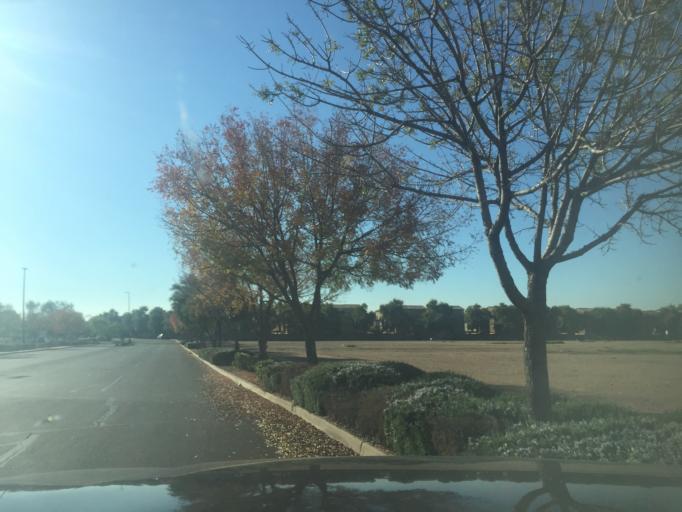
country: US
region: Arizona
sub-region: Maricopa County
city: Tolleson
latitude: 33.4742
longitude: -112.2250
